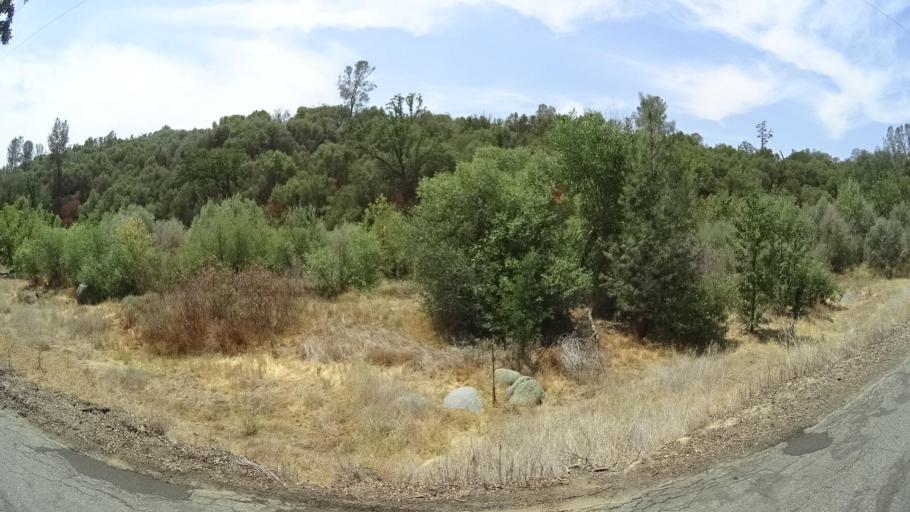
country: US
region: California
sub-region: Mariposa County
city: Mariposa
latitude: 37.4201
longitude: -119.8734
